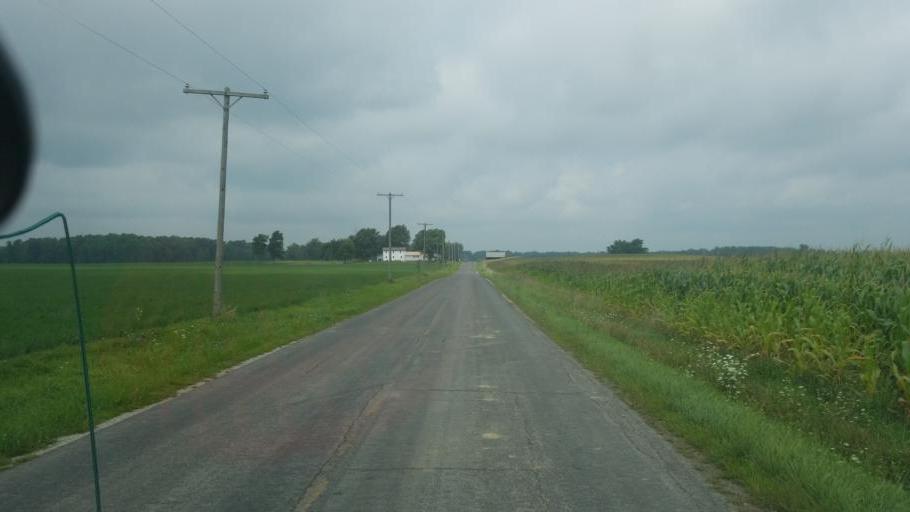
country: US
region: Ohio
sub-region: Huron County
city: Greenwich
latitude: 40.9546
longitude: -82.4597
